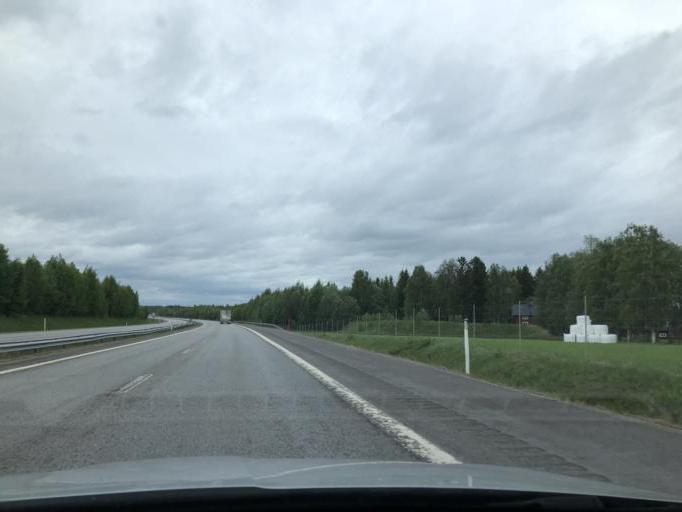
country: SE
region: Norrbotten
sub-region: Pitea Kommun
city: Pitea
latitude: 65.3511
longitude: 21.4379
